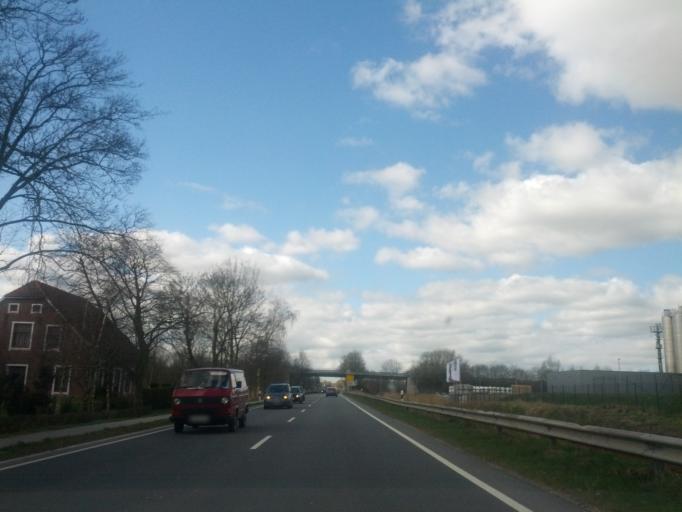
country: DE
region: Lower Saxony
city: Wittmund
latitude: 53.5765
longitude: 7.8044
